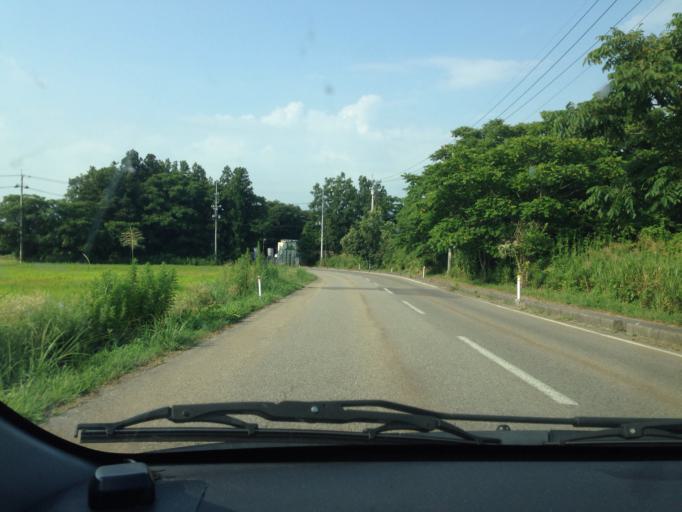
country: JP
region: Fukushima
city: Kitakata
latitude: 37.6888
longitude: 139.8733
